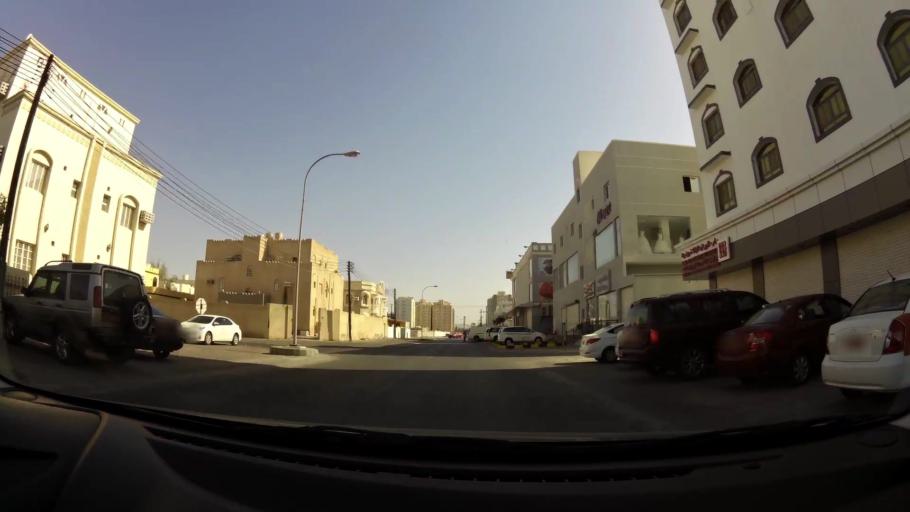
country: OM
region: Muhafazat Masqat
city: As Sib al Jadidah
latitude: 23.6295
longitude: 58.1983
